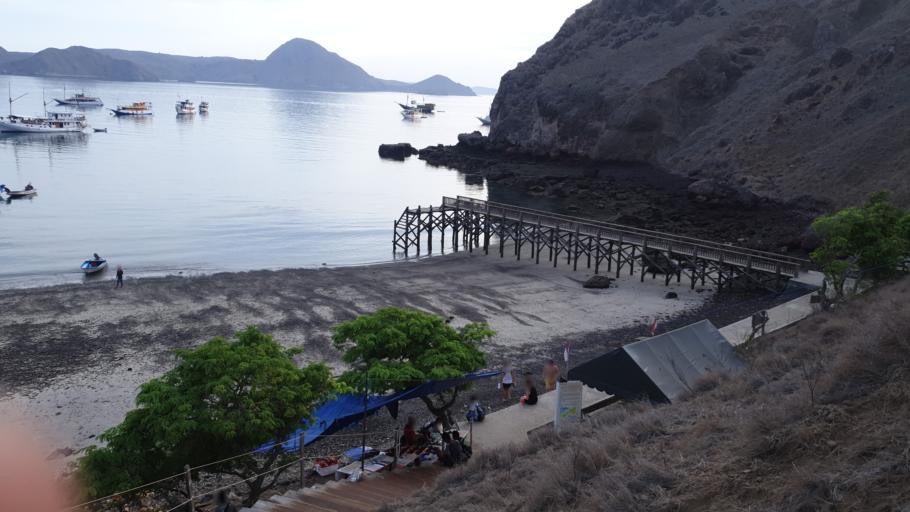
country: ID
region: East Nusa Tenggara
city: Komodo
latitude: -8.6773
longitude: 119.5553
